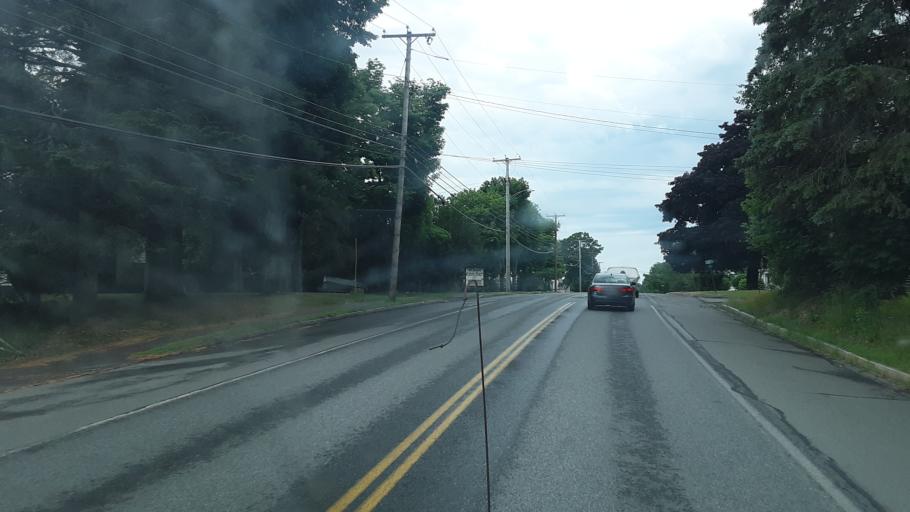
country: US
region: Maine
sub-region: Penobscot County
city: Brewer
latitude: 44.8041
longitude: -68.7449
